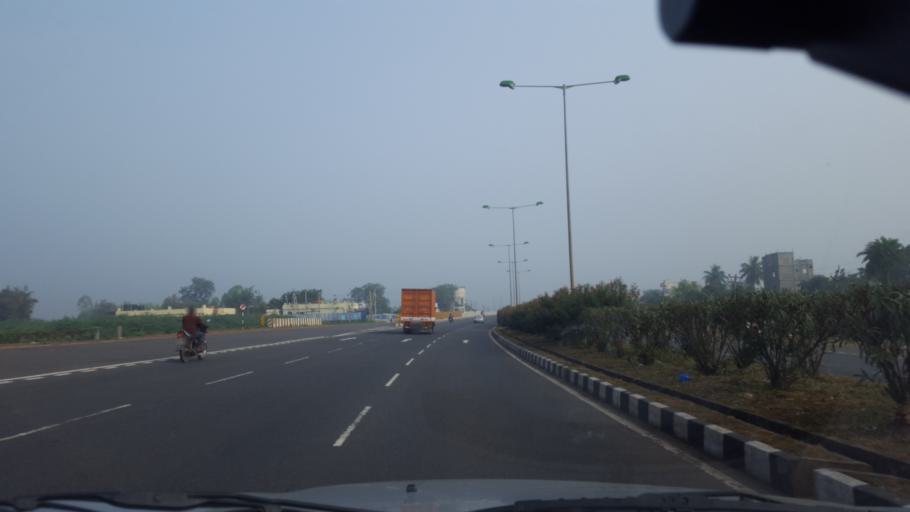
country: IN
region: Andhra Pradesh
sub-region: Prakasam
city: Ongole
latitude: 15.4532
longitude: 80.0469
